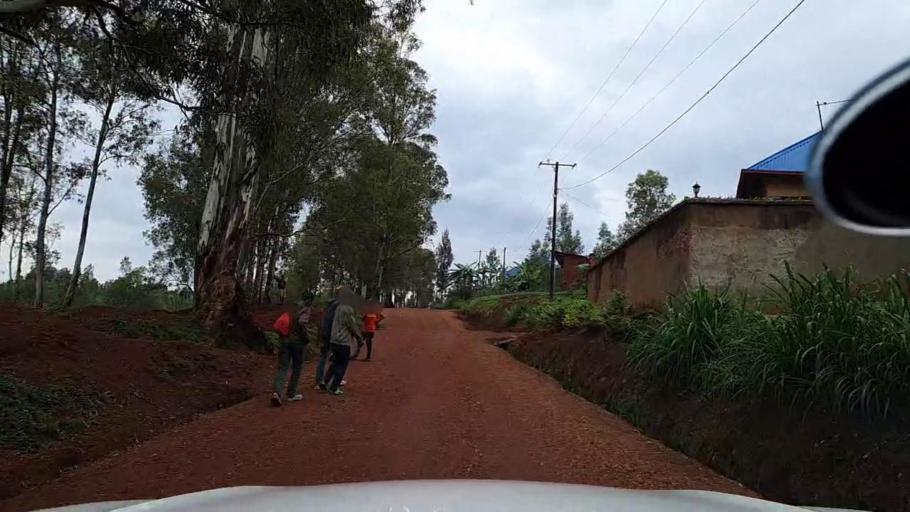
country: RW
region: Kigali
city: Kigali
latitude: -1.9023
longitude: 29.8977
